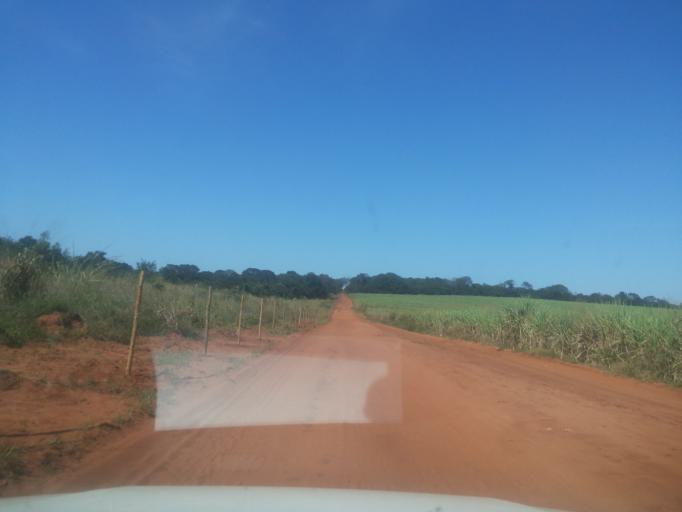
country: BR
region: Minas Gerais
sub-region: Santa Vitoria
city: Santa Vitoria
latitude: -19.0009
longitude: -50.3736
